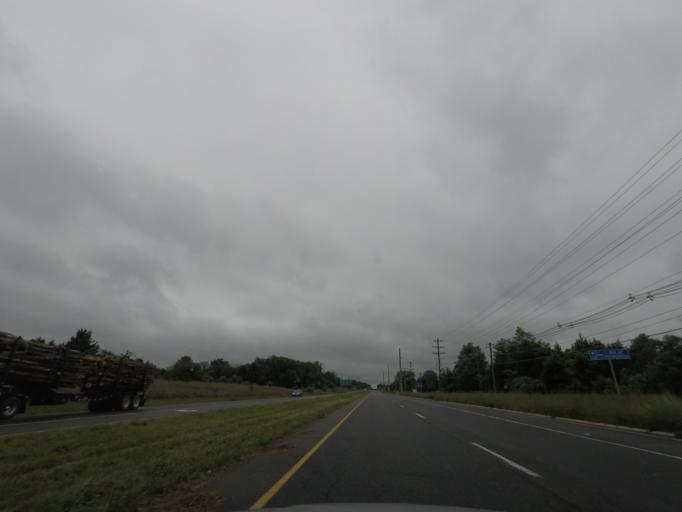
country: US
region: Virginia
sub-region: Prince William County
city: Bull Run Mountain Estates
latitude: 38.8648
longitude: -77.6364
